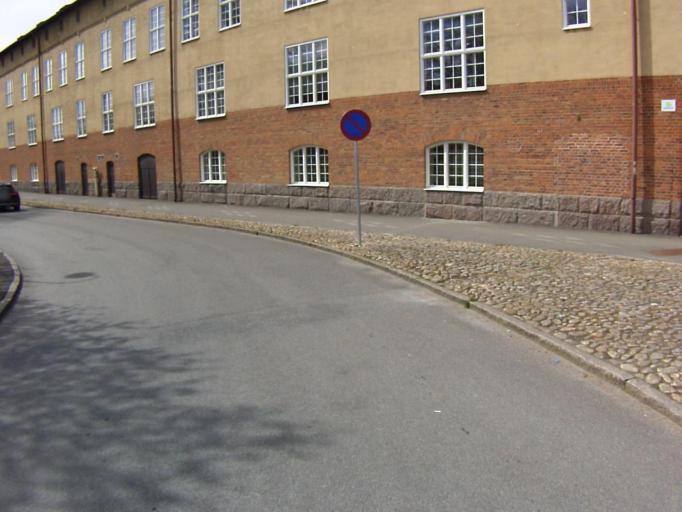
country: SE
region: Skane
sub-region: Kristianstads Kommun
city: Kristianstad
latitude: 56.0488
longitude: 14.1482
